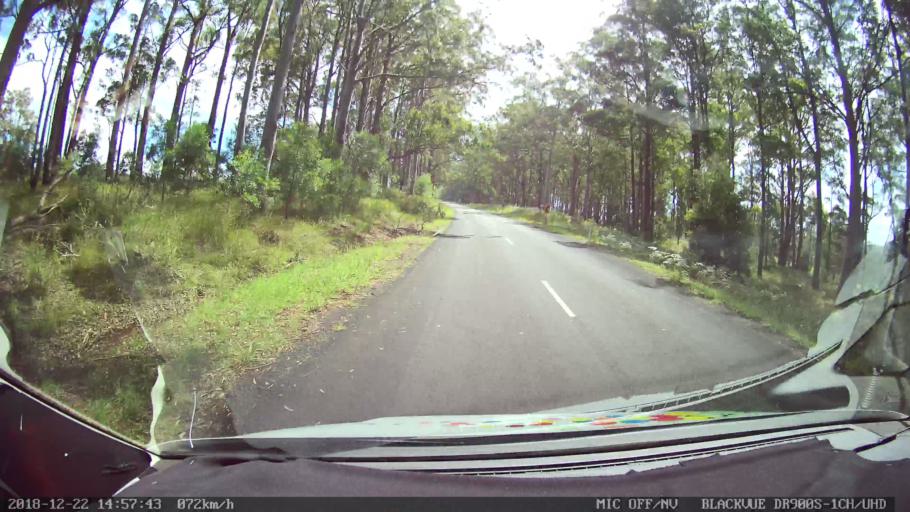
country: AU
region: New South Wales
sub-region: Bellingen
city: Dorrigo
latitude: -30.2359
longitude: 152.4982
